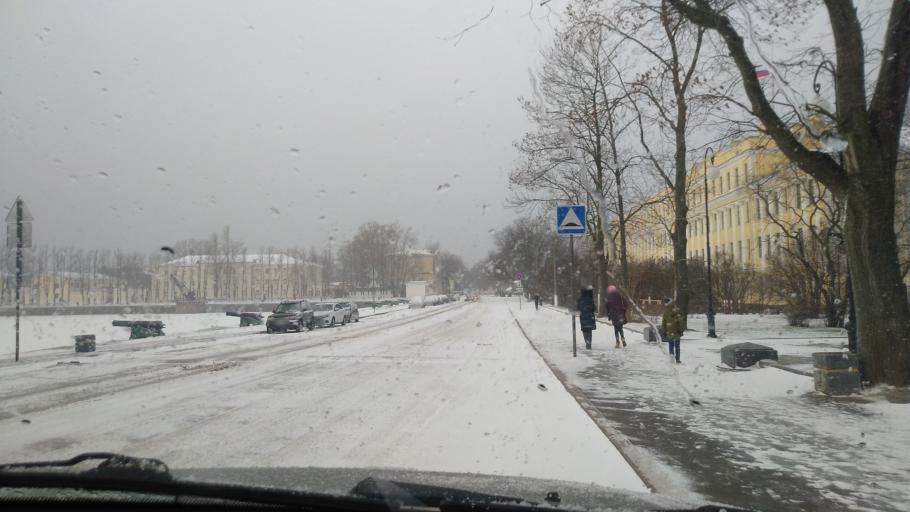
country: RU
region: St.-Petersburg
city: Kronshtadt
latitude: 59.9886
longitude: 29.7655
